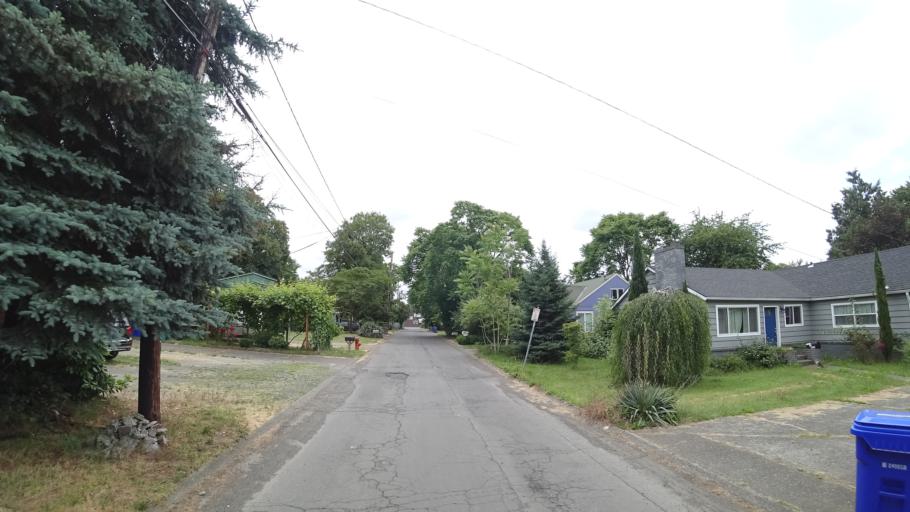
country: US
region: Oregon
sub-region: Multnomah County
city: Lents
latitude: 45.5059
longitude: -122.5705
